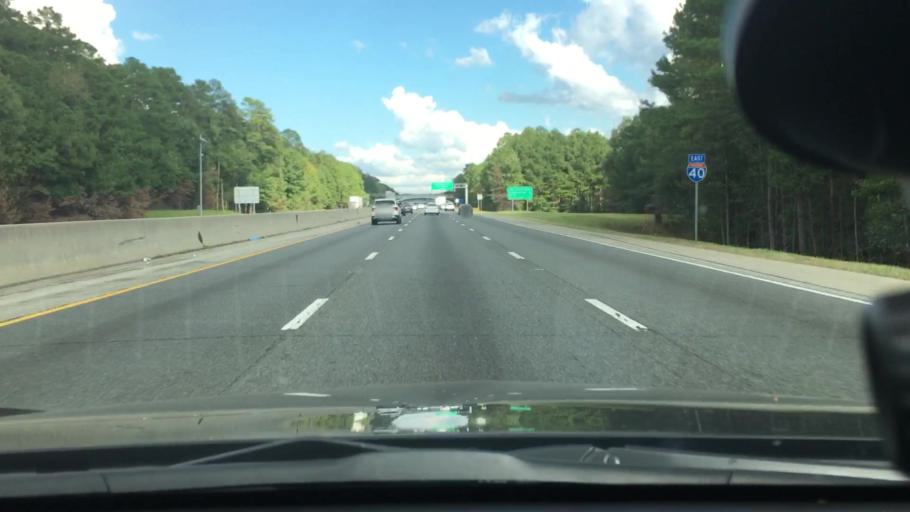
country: US
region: North Carolina
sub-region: Durham County
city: Durham
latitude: 35.9055
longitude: -78.9523
